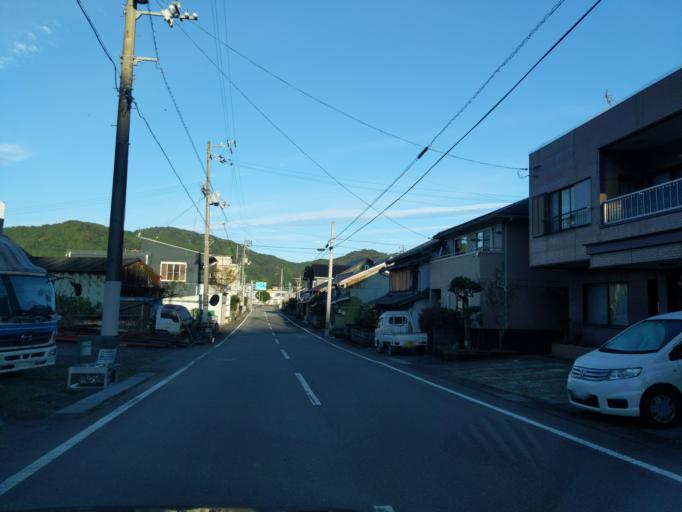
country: JP
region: Kochi
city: Muroto-misakicho
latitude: 33.5435
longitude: 134.2977
